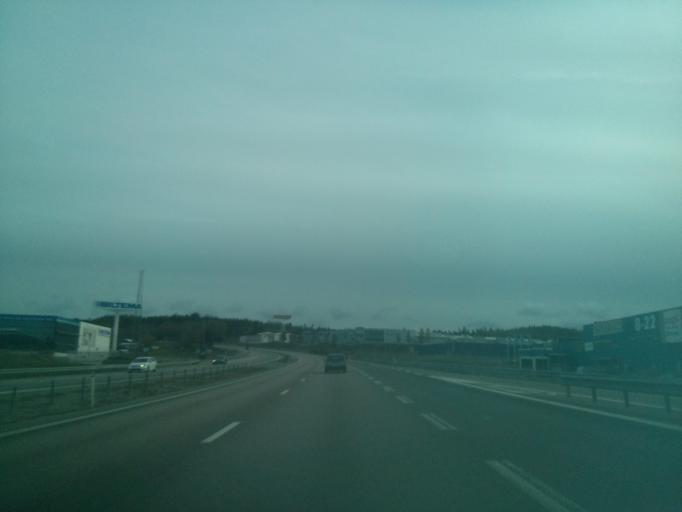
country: SE
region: Vaesternorrland
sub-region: Sundsvalls Kommun
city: Sundsbruk
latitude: 62.4450
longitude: 17.3382
